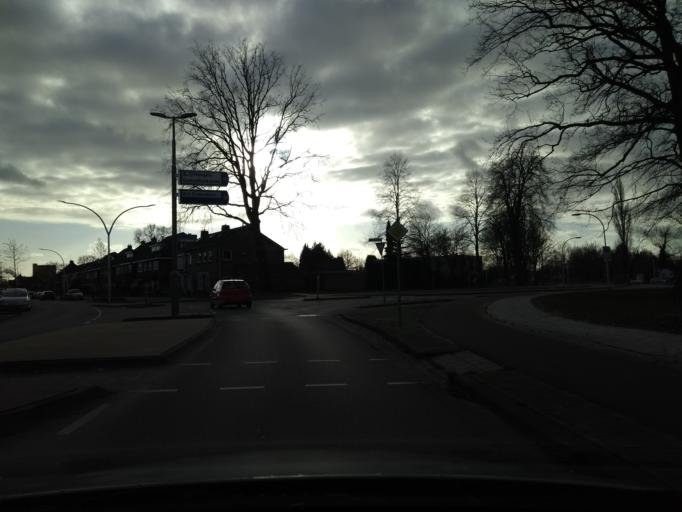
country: NL
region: Overijssel
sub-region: Gemeente Hengelo
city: Hengelo
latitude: 52.2640
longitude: 6.7739
